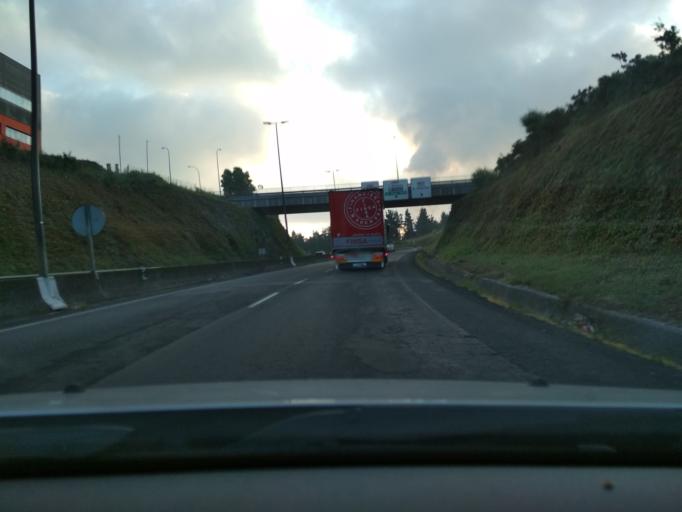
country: ES
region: Galicia
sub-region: Provincia da Coruna
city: Santiago de Compostela
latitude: 42.9052
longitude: -8.5112
